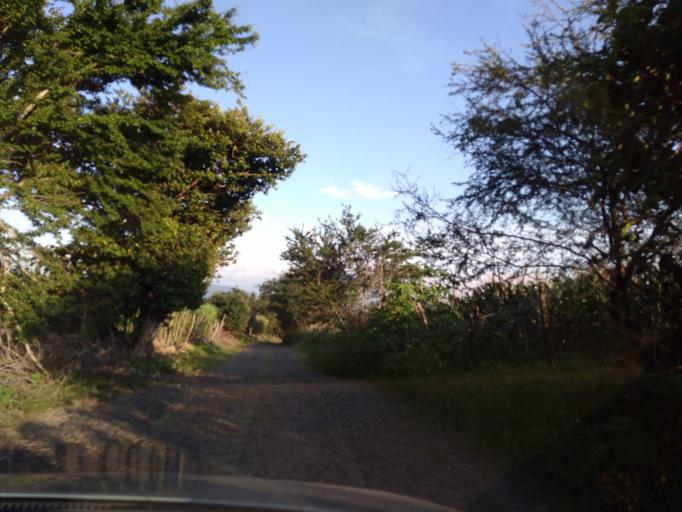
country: MX
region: Jalisco
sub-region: Tonila
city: San Marcos
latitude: 19.4596
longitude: -103.5219
